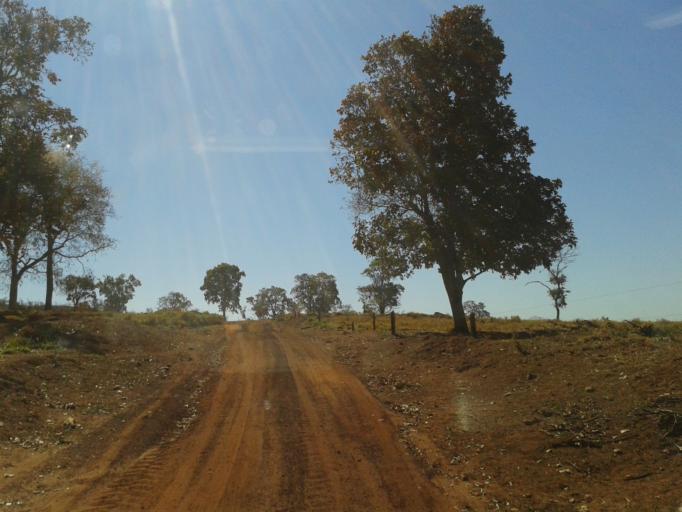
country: BR
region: Minas Gerais
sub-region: Santa Vitoria
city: Santa Vitoria
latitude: -19.1008
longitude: -49.9777
